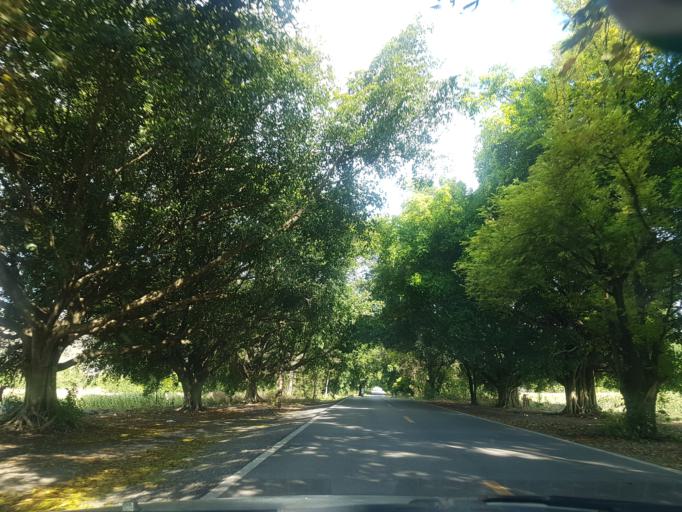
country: TH
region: Lop Buri
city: Lop Buri
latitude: 14.8158
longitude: 100.7515
